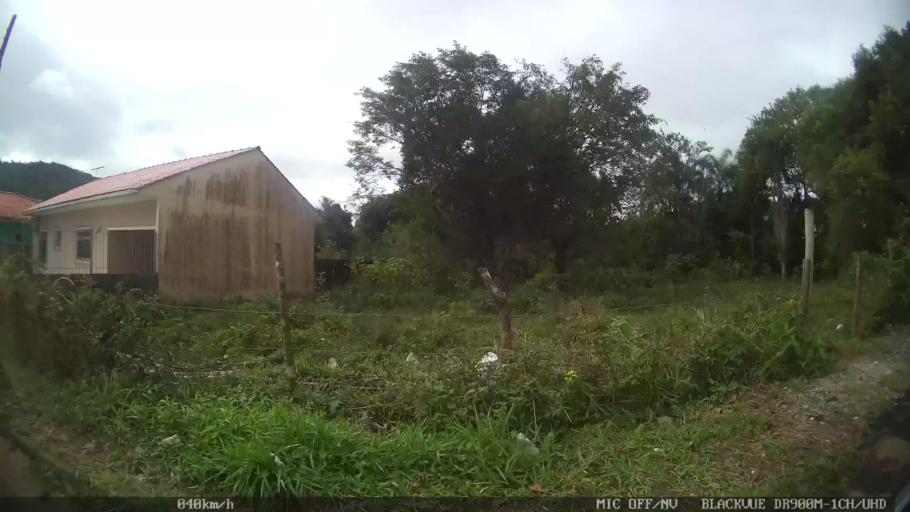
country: BR
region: Santa Catarina
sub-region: Biguacu
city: Biguacu
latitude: -27.5286
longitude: -48.6453
